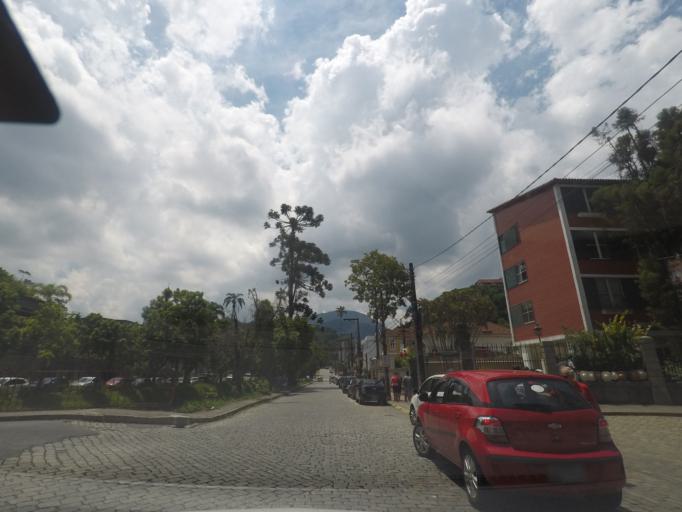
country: BR
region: Rio de Janeiro
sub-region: Petropolis
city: Petropolis
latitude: -22.5077
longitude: -43.1767
